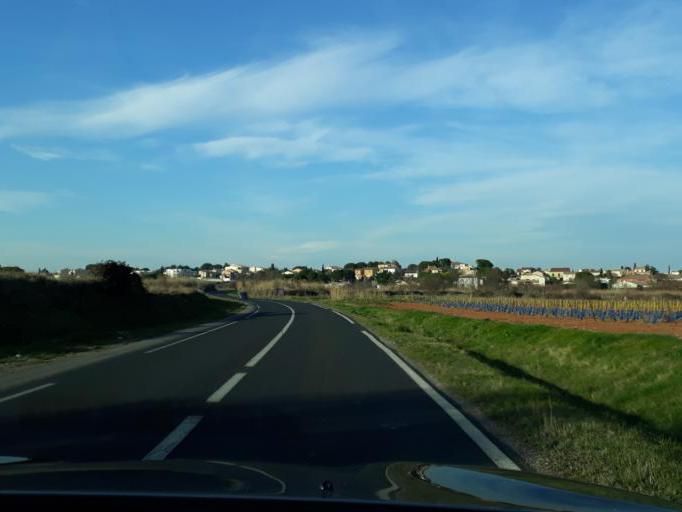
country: FR
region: Languedoc-Roussillon
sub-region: Departement de l'Herault
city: Marseillan
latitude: 43.3446
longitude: 3.5259
